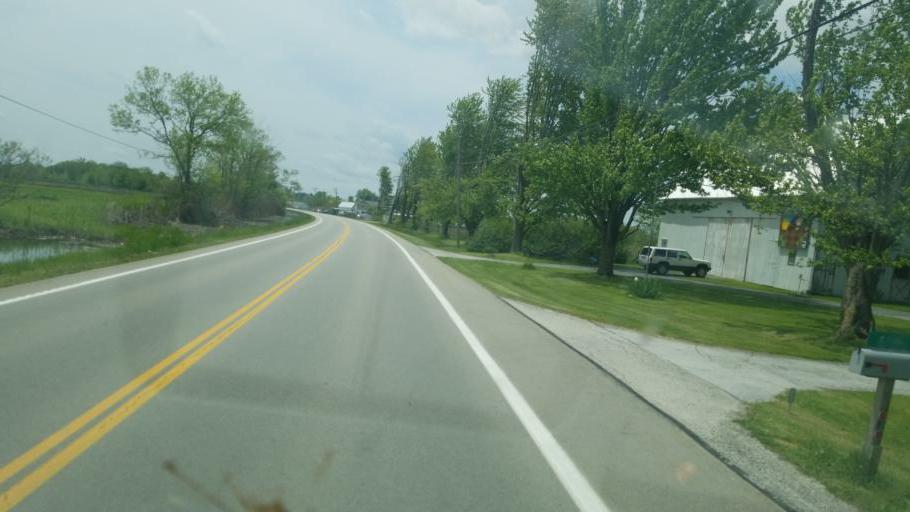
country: US
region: Ohio
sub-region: Ottawa County
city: Oak Harbor
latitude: 41.4659
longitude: -83.0449
